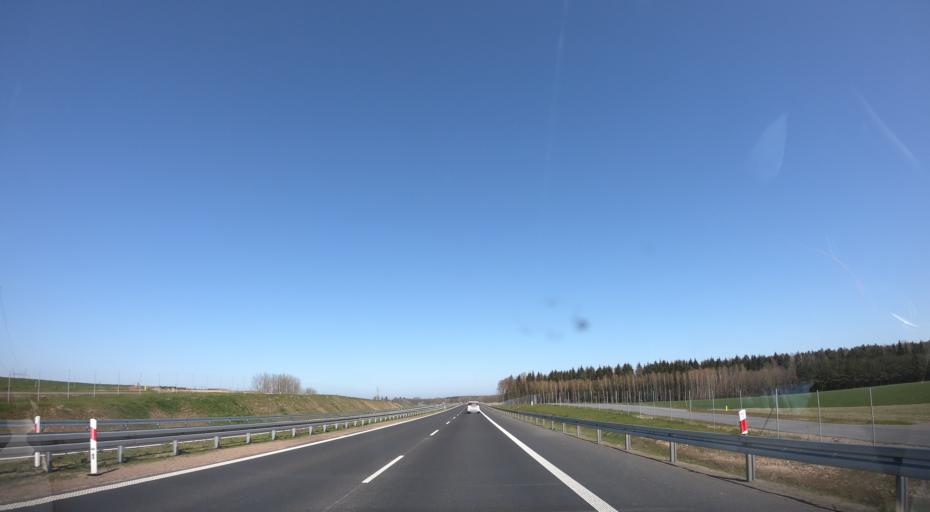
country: PL
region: West Pomeranian Voivodeship
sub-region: Powiat goleniowski
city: Przybiernow
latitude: 53.7974
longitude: 14.7765
